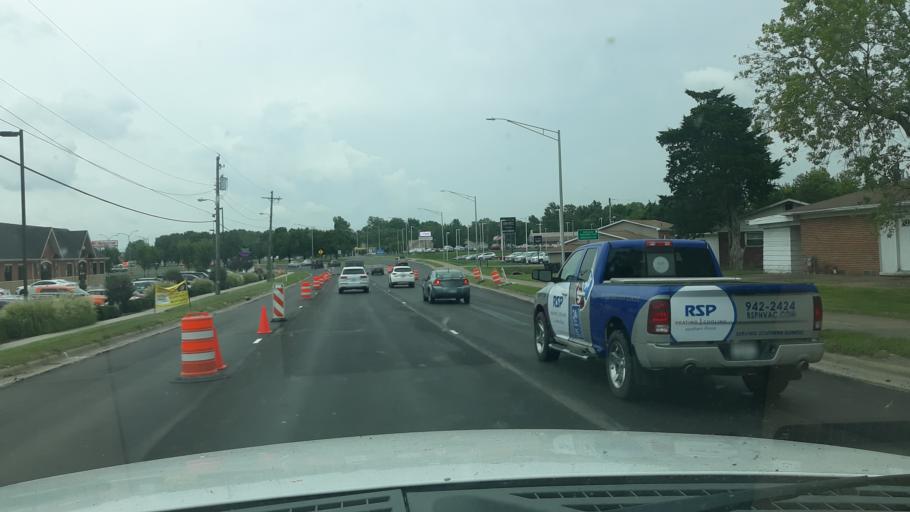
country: US
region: Illinois
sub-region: Jackson County
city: Carbondale
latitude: 37.7267
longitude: -89.2024
